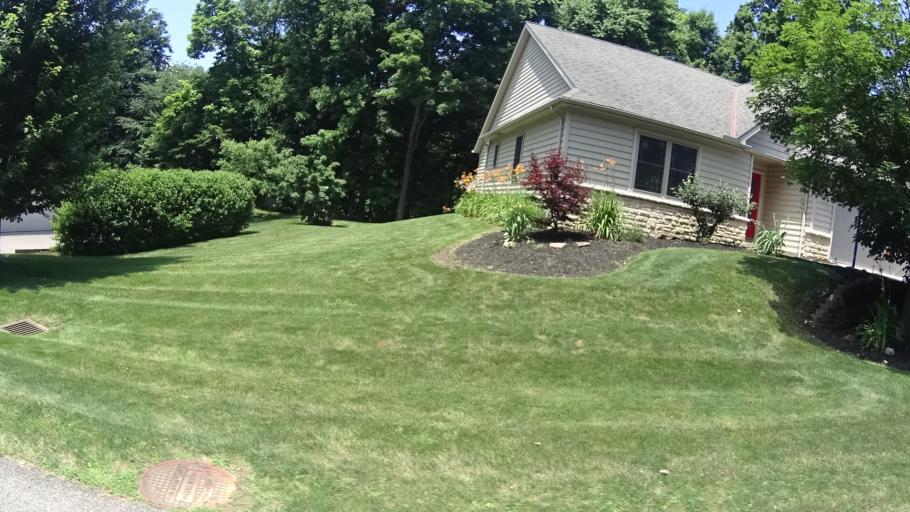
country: US
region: Ohio
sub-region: Lorain County
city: Vermilion
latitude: 41.3357
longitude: -82.3484
